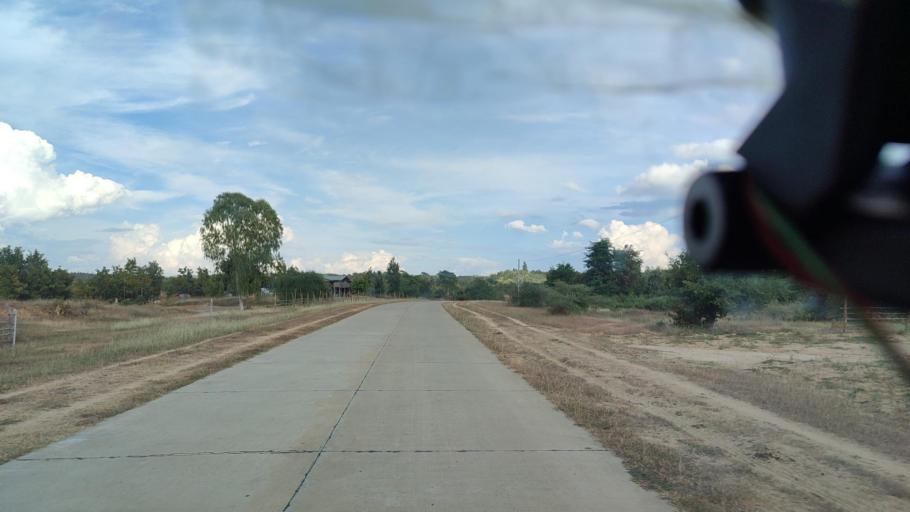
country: MM
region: Mandalay
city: Yamethin
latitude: 20.0962
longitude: 96.0254
